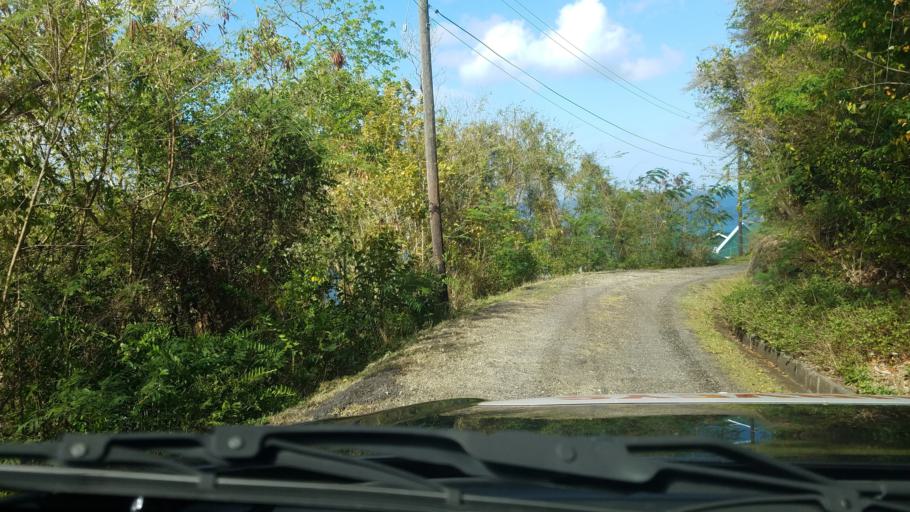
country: LC
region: Castries Quarter
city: Castries
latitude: 14.0209
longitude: -61.0006
